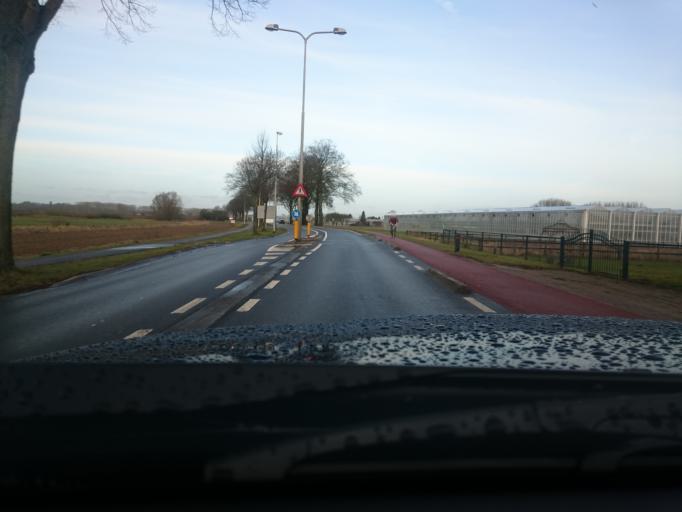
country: NL
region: Gelderland
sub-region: Gemeente Zutphen
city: Zutphen
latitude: 52.1460
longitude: 6.1702
